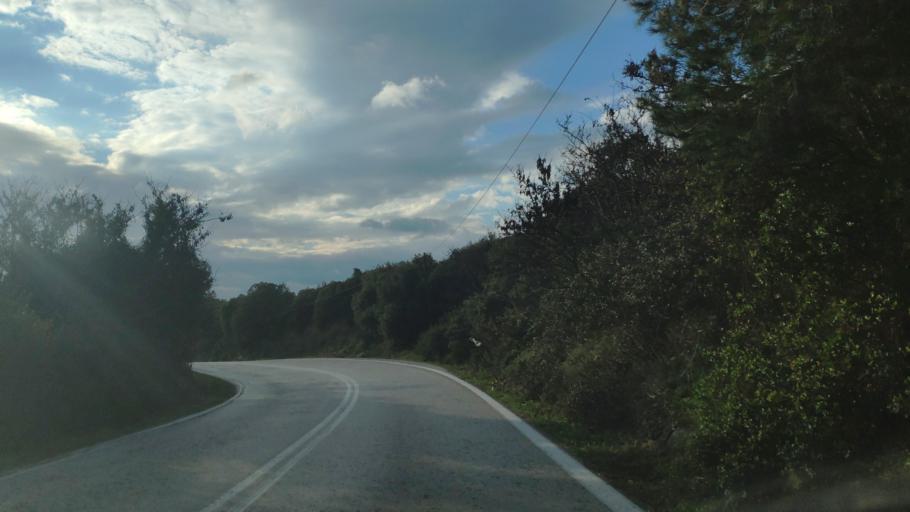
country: GR
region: Peloponnese
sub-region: Nomos Korinthias
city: Nemea
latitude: 37.7797
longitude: 22.7229
